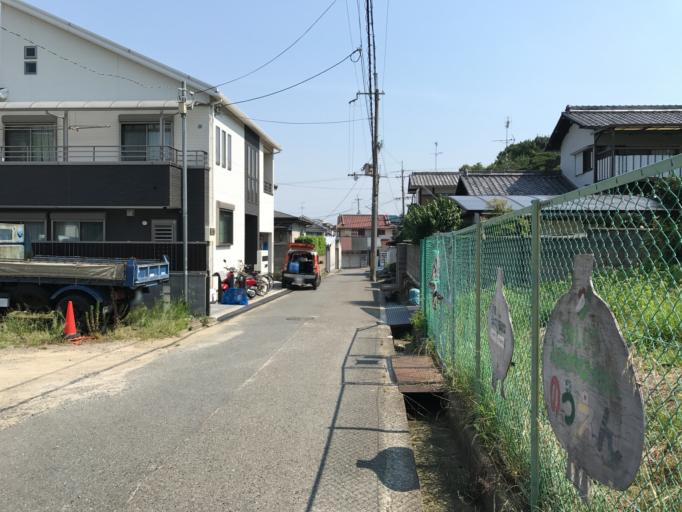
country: JP
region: Osaka
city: Kashihara
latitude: 34.6068
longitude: 135.6342
